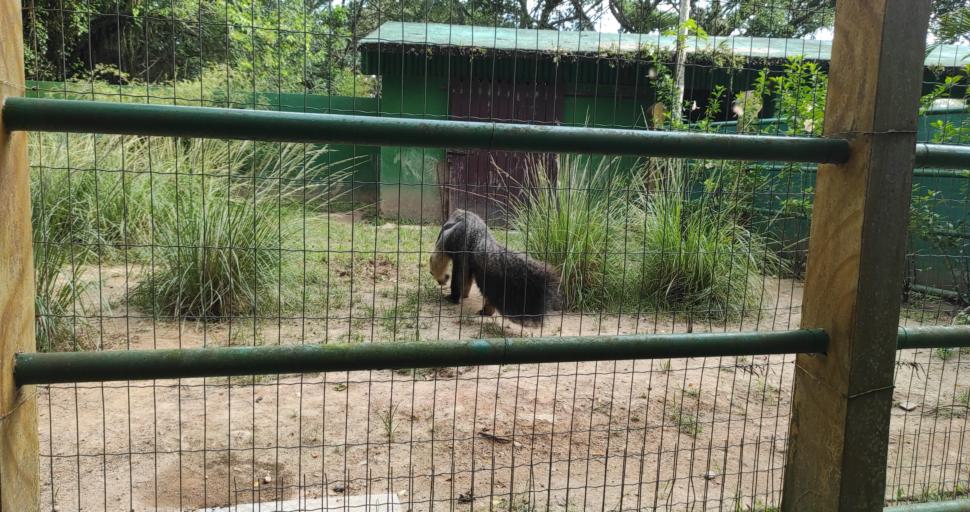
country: BR
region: Santa Catarina
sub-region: Penha
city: Penha
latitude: -26.8018
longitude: -48.6177
